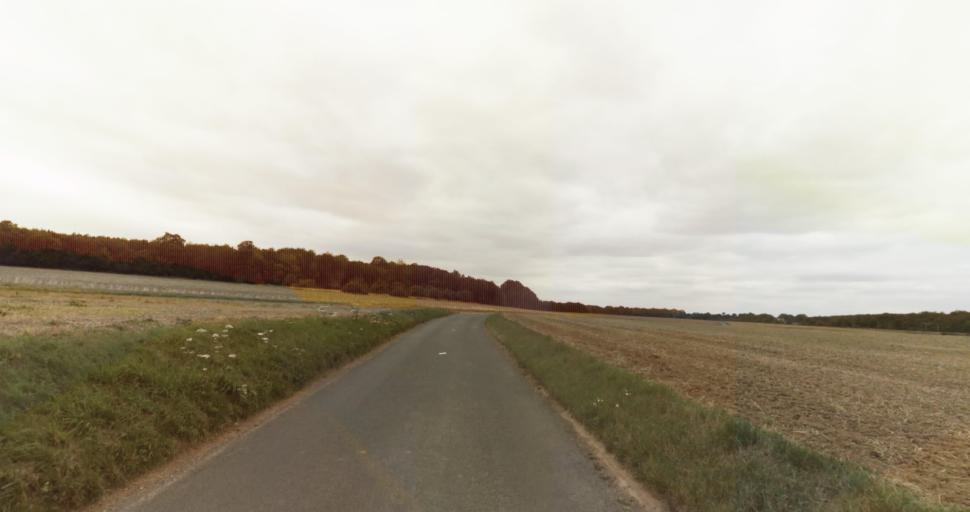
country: FR
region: Haute-Normandie
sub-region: Departement de l'Eure
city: Evreux
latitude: 48.9876
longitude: 1.2320
